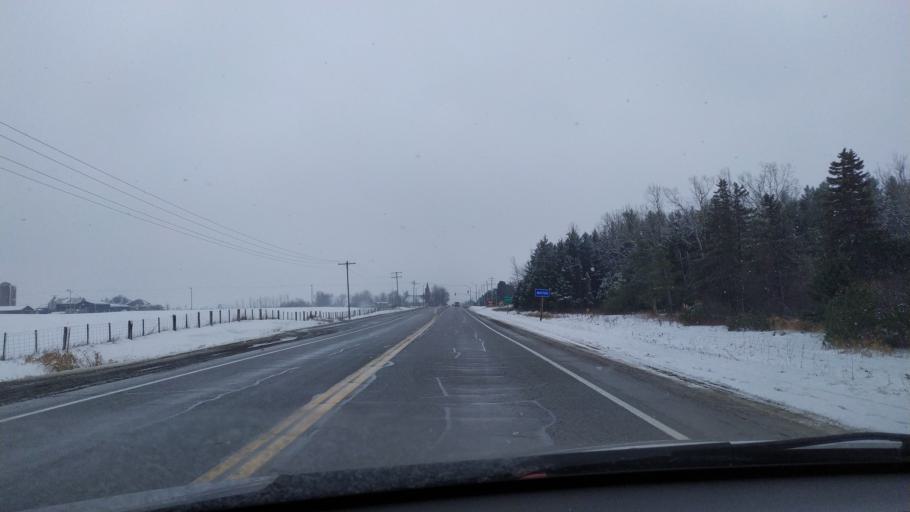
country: CA
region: Ontario
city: Waterloo
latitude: 43.6252
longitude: -80.6983
